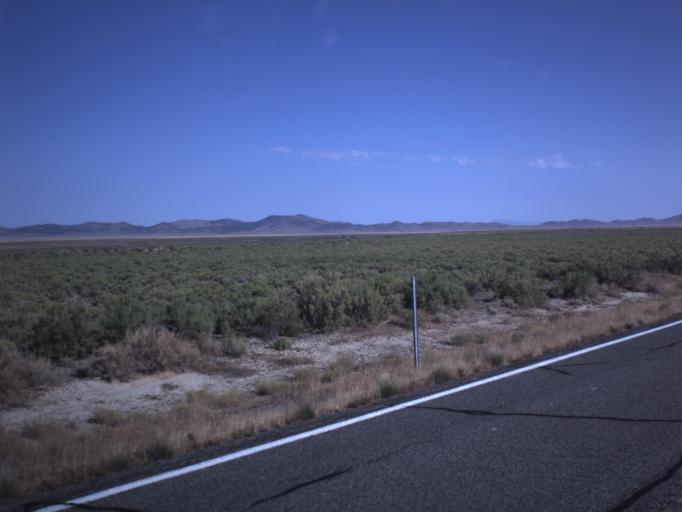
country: US
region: Utah
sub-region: Beaver County
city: Milford
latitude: 38.5149
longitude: -112.9911
